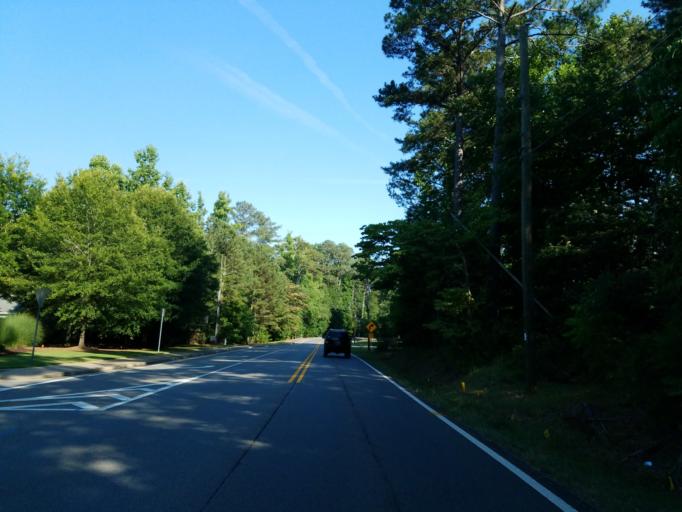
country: US
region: Georgia
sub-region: Fulton County
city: Milton
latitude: 34.1155
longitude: -84.3392
